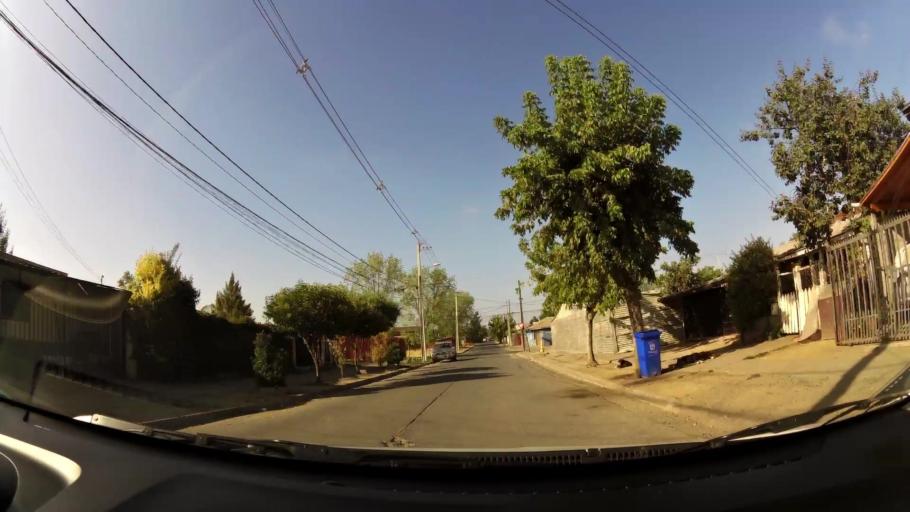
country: CL
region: Maule
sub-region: Provincia de Talca
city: Talca
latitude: -35.4047
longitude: -71.6601
